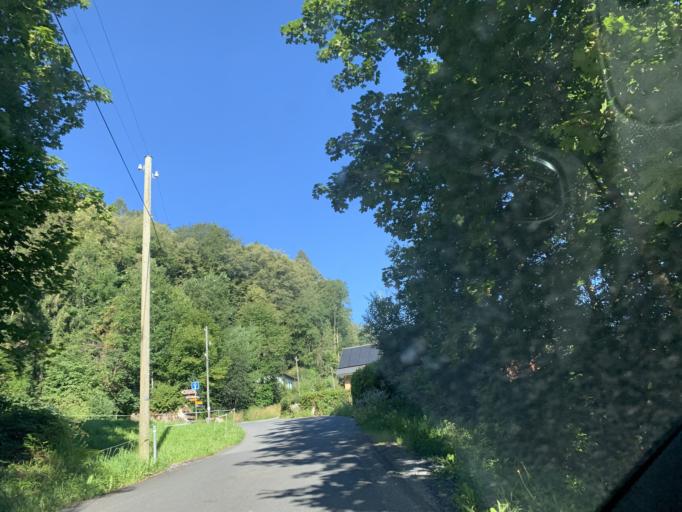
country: CH
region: Saint Gallen
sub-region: Wahlkreis Sarganserland
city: Quarten
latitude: 47.1094
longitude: 9.2129
